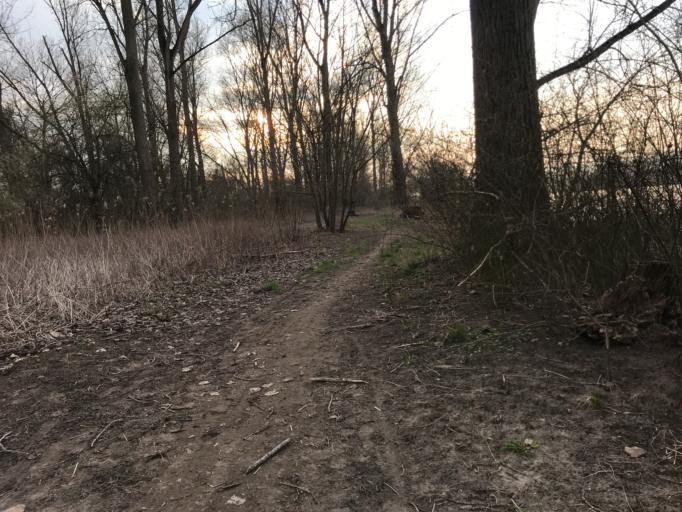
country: DE
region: Rheinland-Pfalz
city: Budenheim
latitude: 50.0337
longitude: 8.1996
